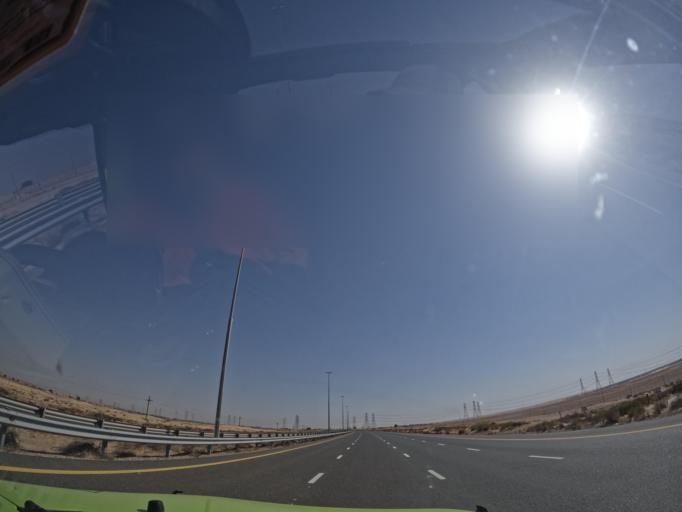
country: AE
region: Ash Shariqah
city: Sharjah
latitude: 25.0142
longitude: 55.5378
